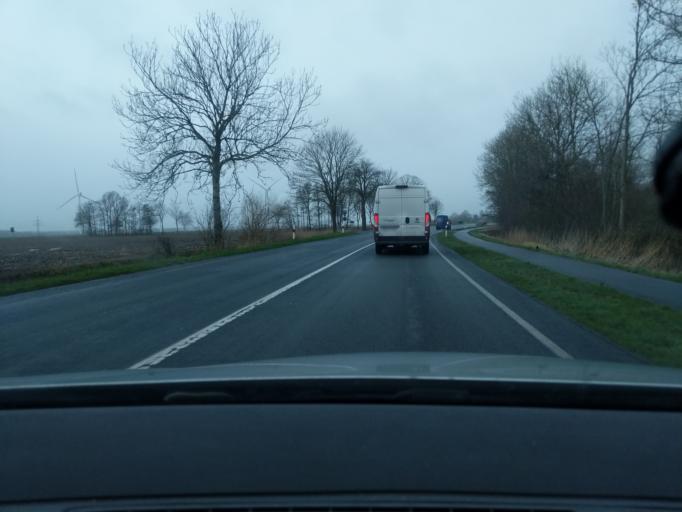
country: DE
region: Lower Saxony
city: Wanna
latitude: 53.8139
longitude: 8.7691
